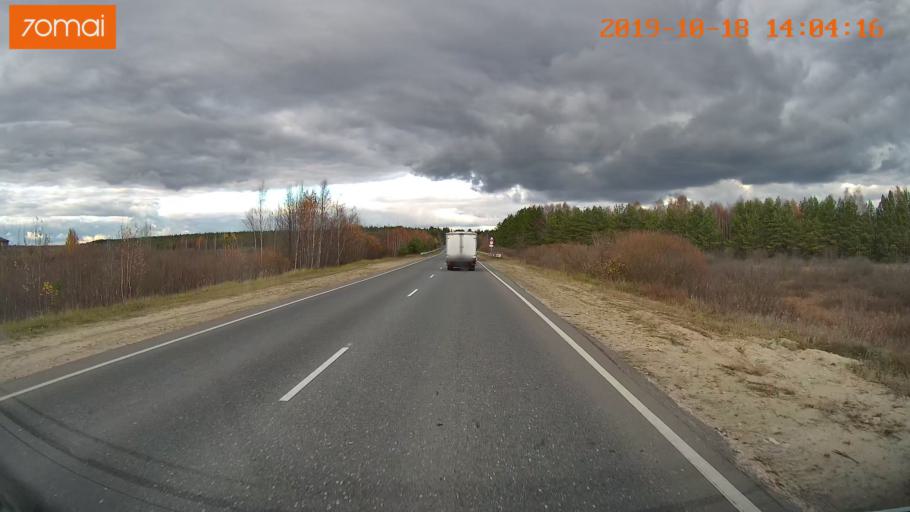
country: RU
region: Rjazan
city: Spas-Klepiki
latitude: 55.1240
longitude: 40.1335
